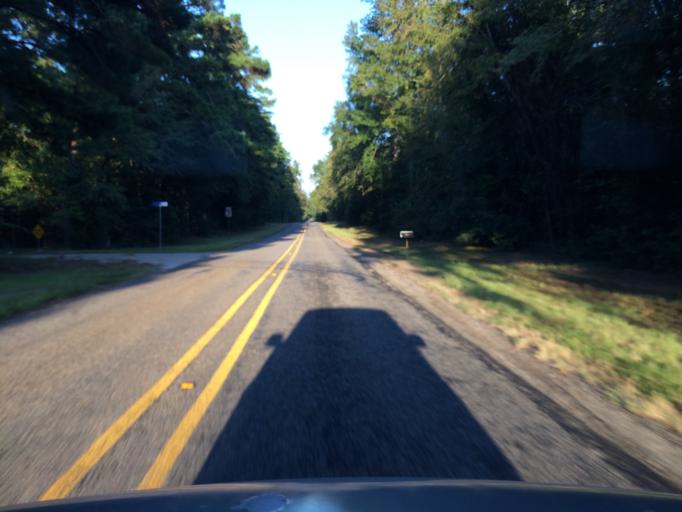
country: US
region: Texas
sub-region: Wood County
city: Hawkins
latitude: 32.7418
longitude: -95.2805
